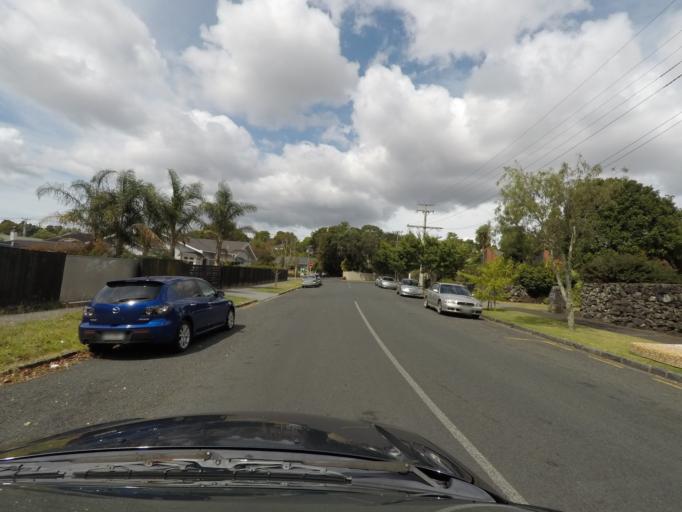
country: NZ
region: Auckland
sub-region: Auckland
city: Rosebank
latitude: -36.8844
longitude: 174.7094
